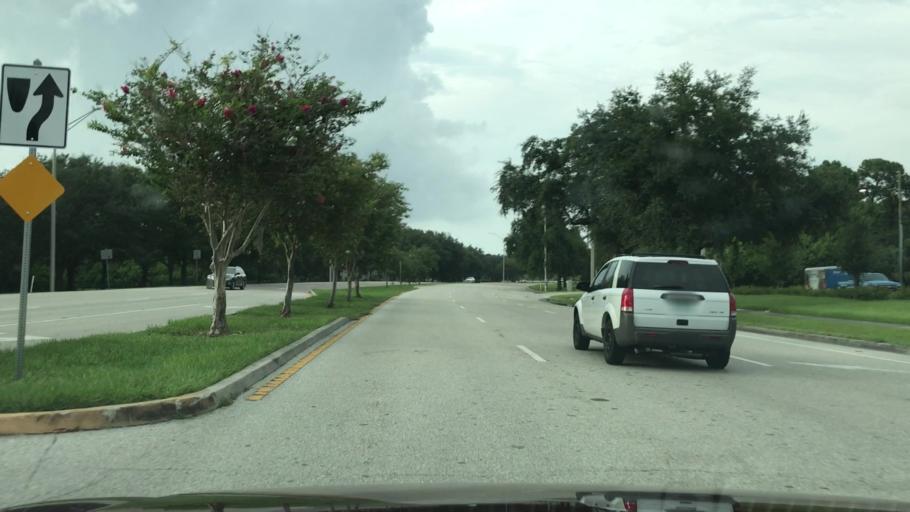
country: US
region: Florida
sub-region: Sarasota County
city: Venice Gardens
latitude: 27.0811
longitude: -82.3888
